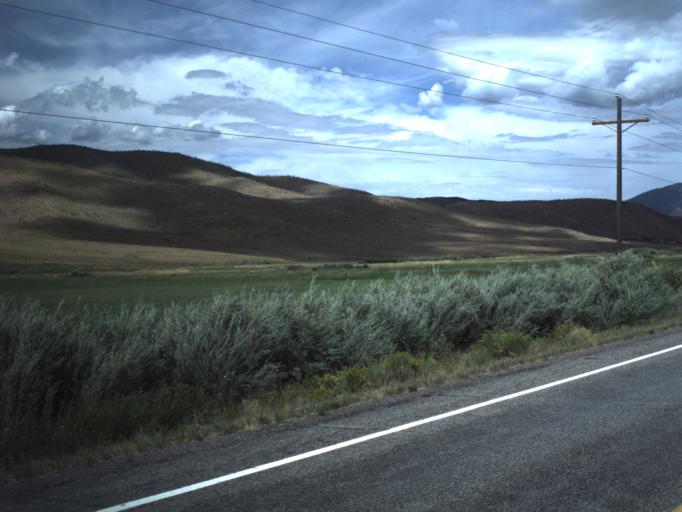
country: US
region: Utah
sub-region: Sanpete County
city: Fairview
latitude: 39.8250
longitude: -111.5100
